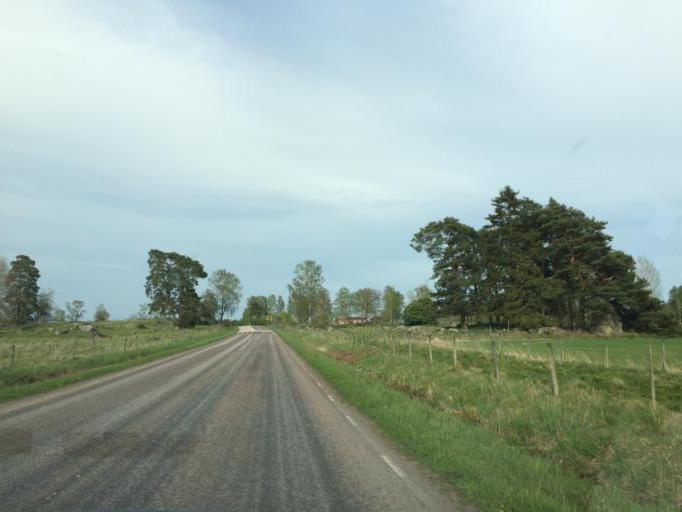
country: SE
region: Vaestmanland
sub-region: Hallstahammars Kommun
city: Hallstahammar
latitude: 59.6028
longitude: 16.1906
